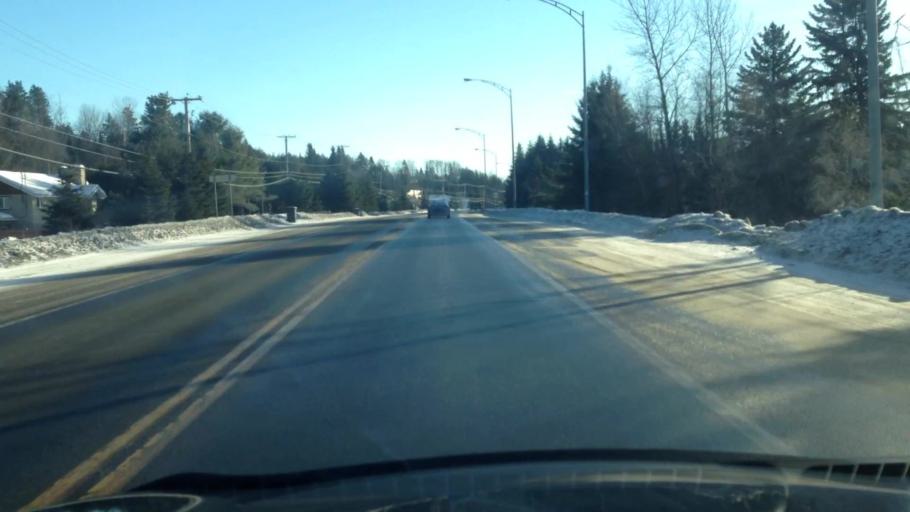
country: CA
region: Quebec
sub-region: Laurentides
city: Saint-Sauveur
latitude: 45.9076
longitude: -74.2554
